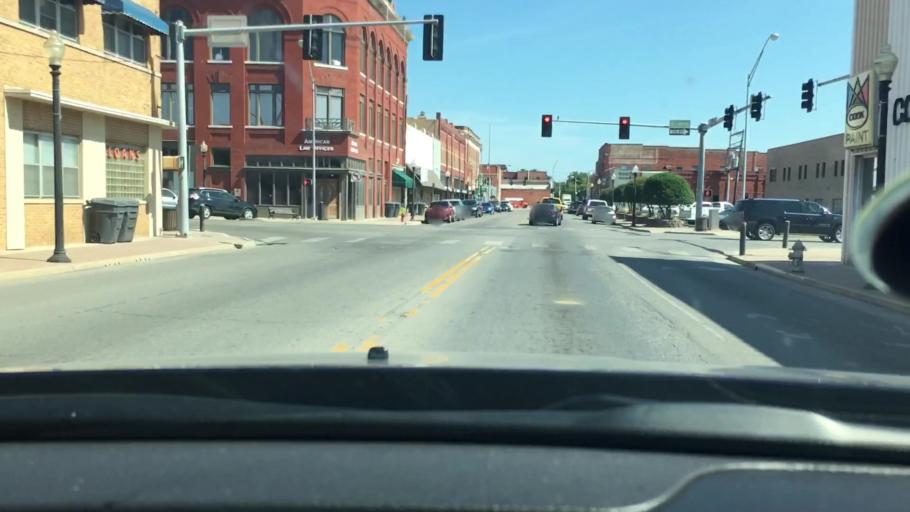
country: US
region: Oklahoma
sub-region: Carter County
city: Ardmore
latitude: 34.1722
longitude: -97.1285
